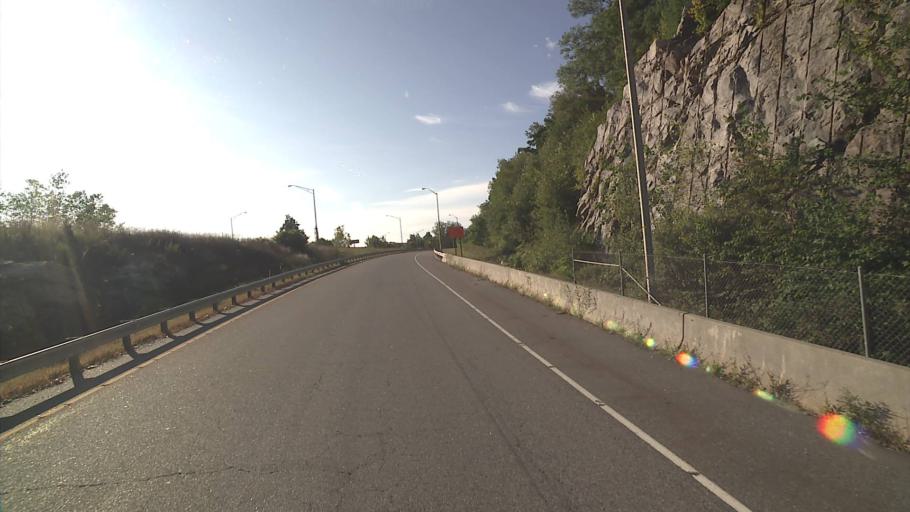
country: US
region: Connecticut
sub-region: New London County
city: Norwich
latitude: 41.5566
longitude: -72.1193
